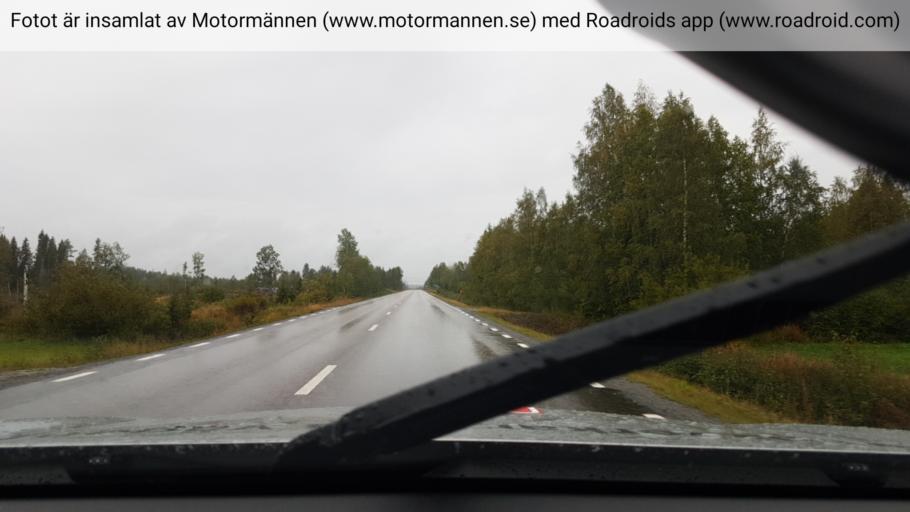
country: SE
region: Vaesterbotten
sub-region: Vannas Kommun
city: Vaennaes
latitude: 63.9119
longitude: 19.6676
